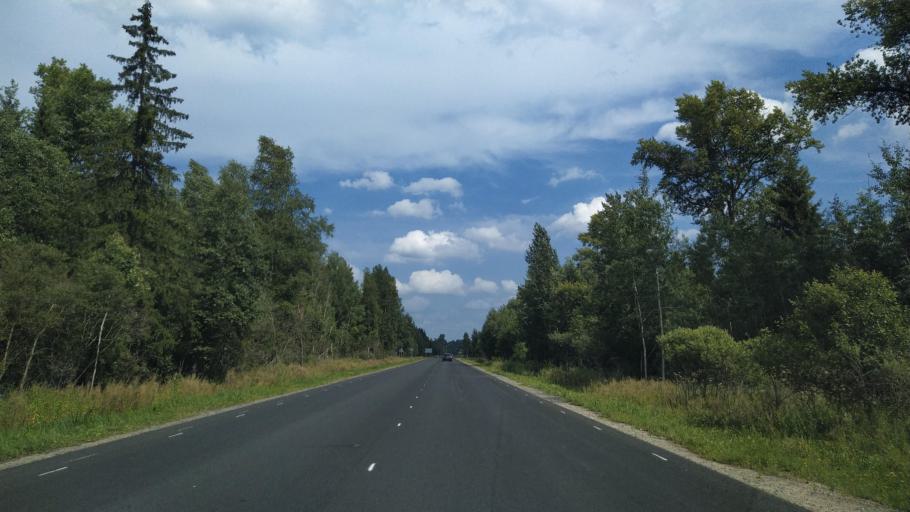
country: RU
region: Pskov
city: Vybor
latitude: 57.7079
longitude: 28.8940
